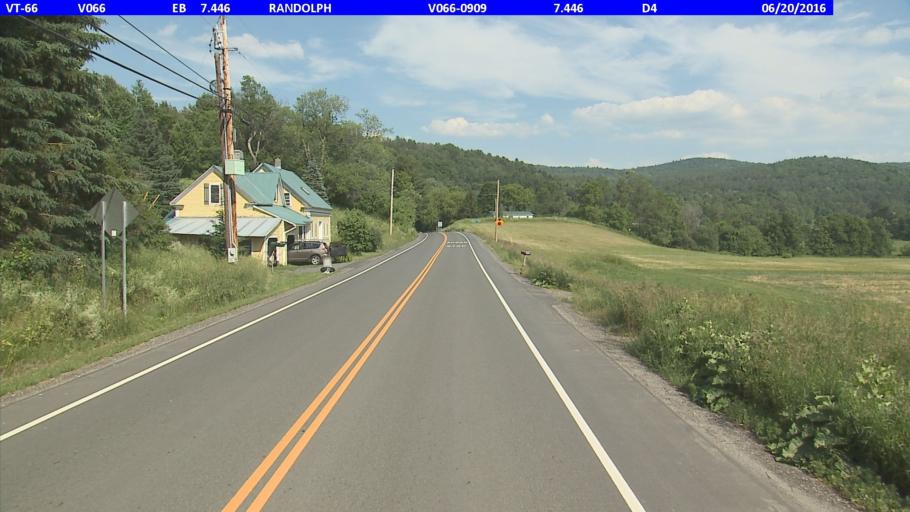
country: US
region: Vermont
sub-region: Orange County
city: Randolph
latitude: 43.9407
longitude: -72.5576
